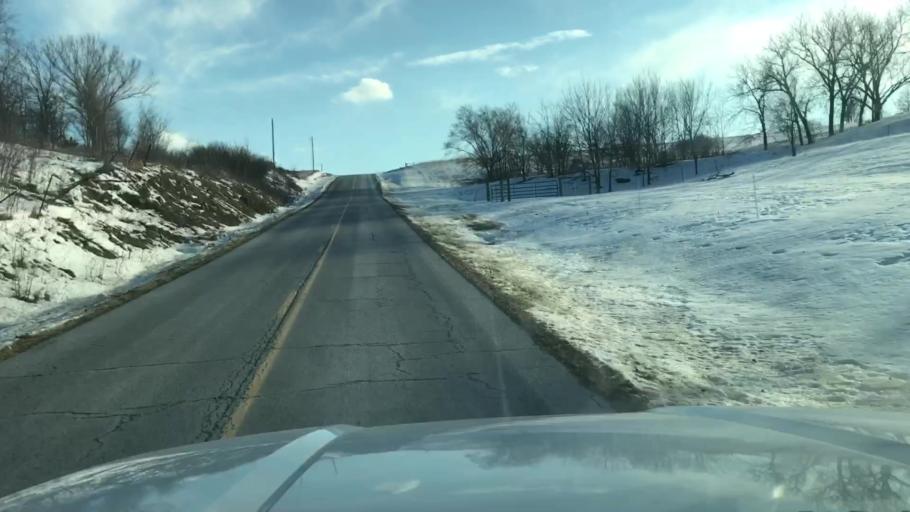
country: US
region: Missouri
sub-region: Holt County
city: Oregon
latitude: 40.0708
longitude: -94.9747
